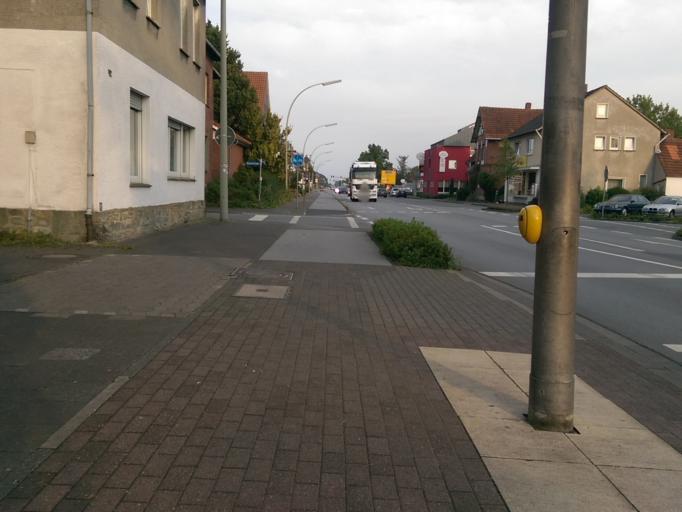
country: DE
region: North Rhine-Westphalia
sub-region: Regierungsbezirk Detmold
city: Rheda-Wiedenbruck
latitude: 51.8810
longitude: 8.2367
